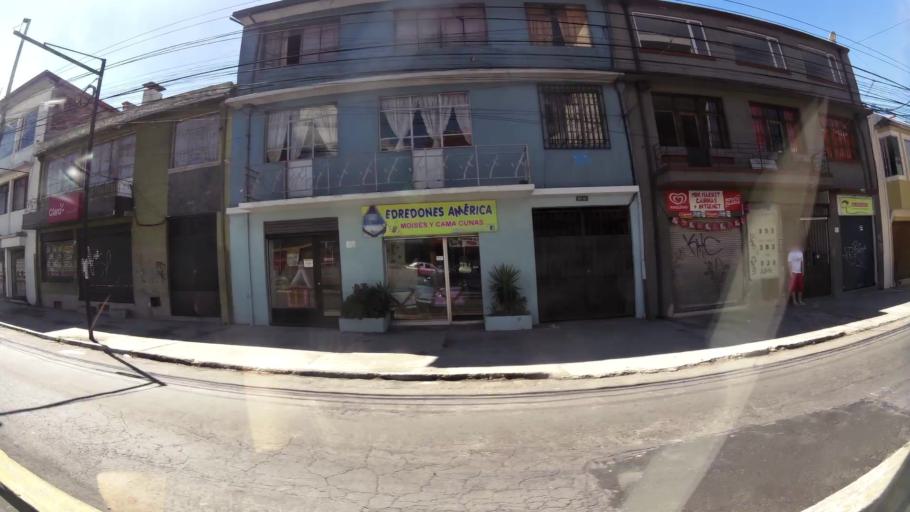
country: EC
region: Pichincha
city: Quito
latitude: -0.1878
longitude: -78.4958
